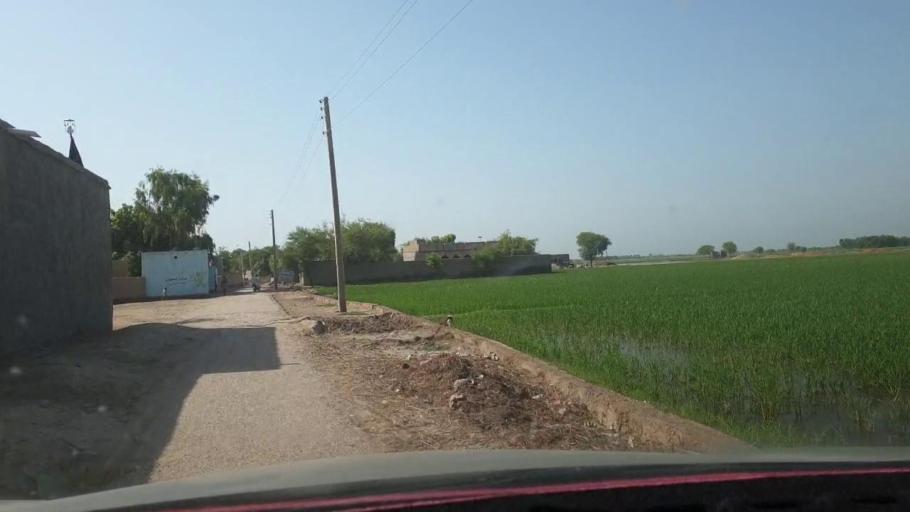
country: PK
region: Sindh
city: Nasirabad
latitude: 27.3834
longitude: 67.8784
